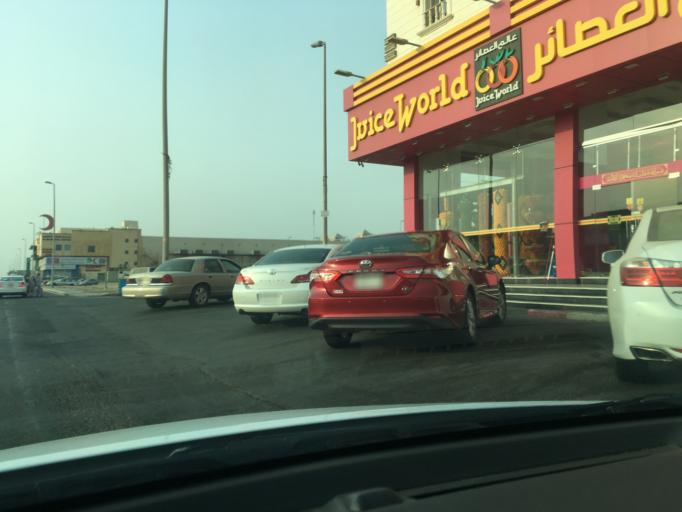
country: SA
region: Makkah
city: Jeddah
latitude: 21.7548
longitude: 39.1862
